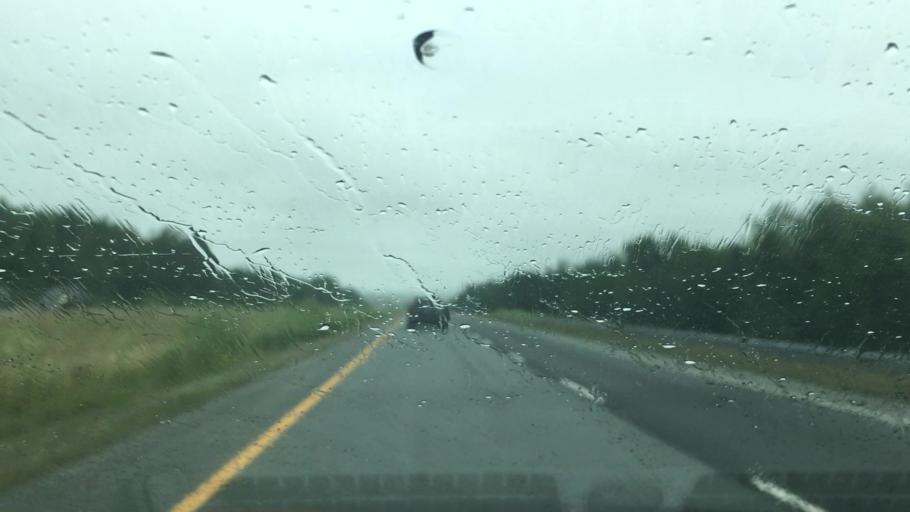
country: CA
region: Nova Scotia
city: Truro
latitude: 45.2361
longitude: -63.2943
